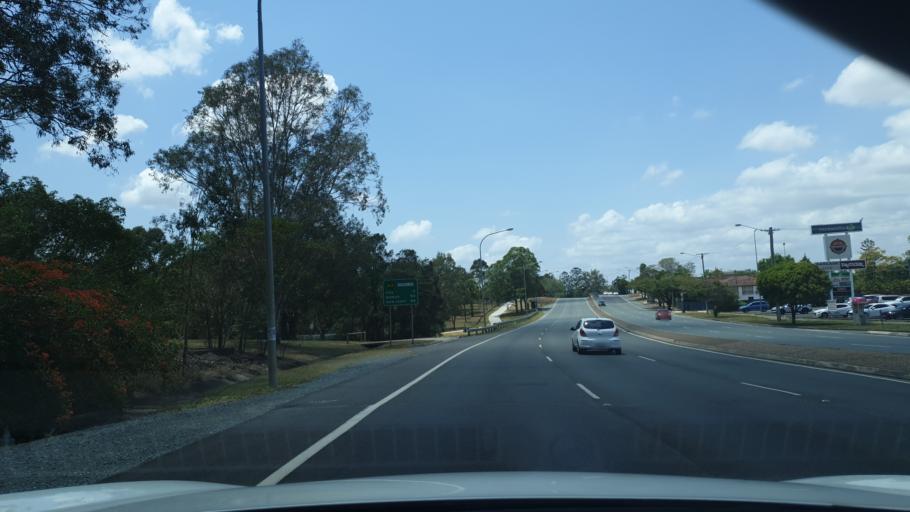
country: AU
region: Queensland
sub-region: Brisbane
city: Chermside West
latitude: -27.3744
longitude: 153.0251
